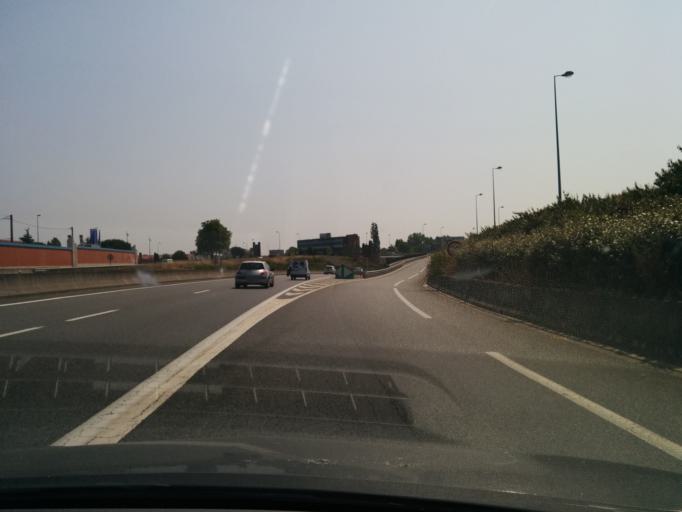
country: FR
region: Midi-Pyrenees
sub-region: Departement du Tarn
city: Le Sequestre
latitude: 43.9182
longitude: 2.1147
